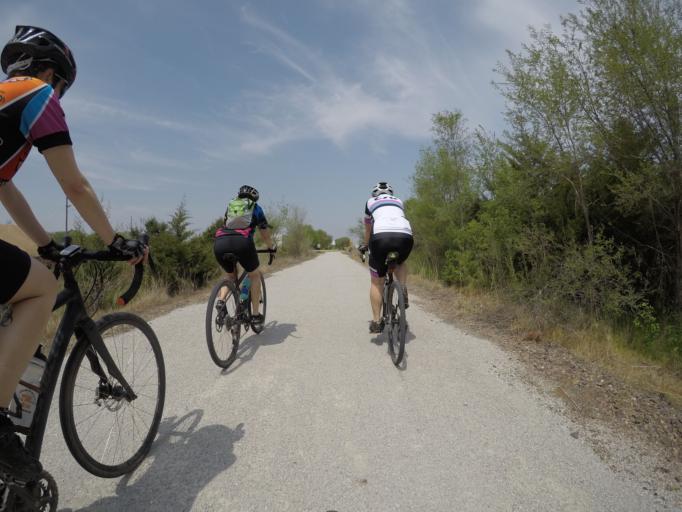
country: US
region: Nebraska
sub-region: Gage County
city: Beatrice
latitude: 40.2570
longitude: -96.7392
